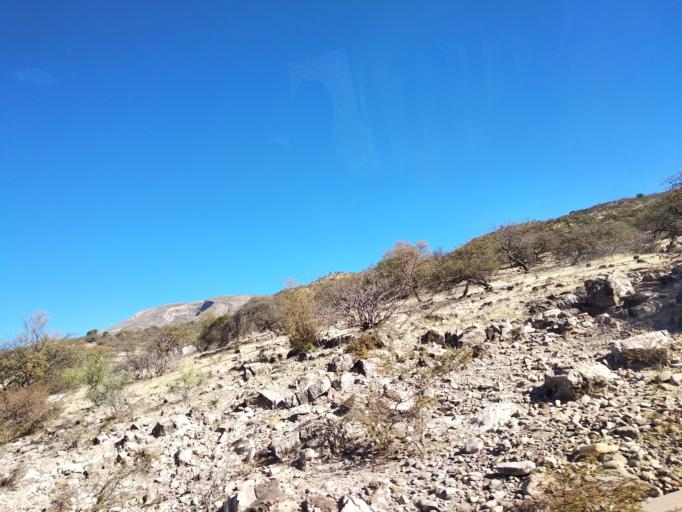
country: BO
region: Cochabamba
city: Mizque
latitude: -18.0820
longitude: -65.7465
